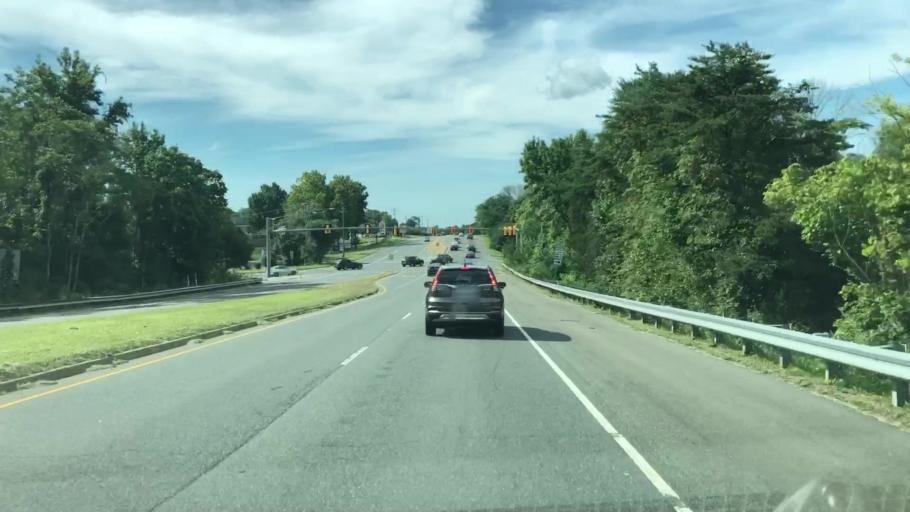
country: US
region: Virginia
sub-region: City of Fredericksburg
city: Fredericksburg
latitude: 38.3018
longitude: -77.4469
